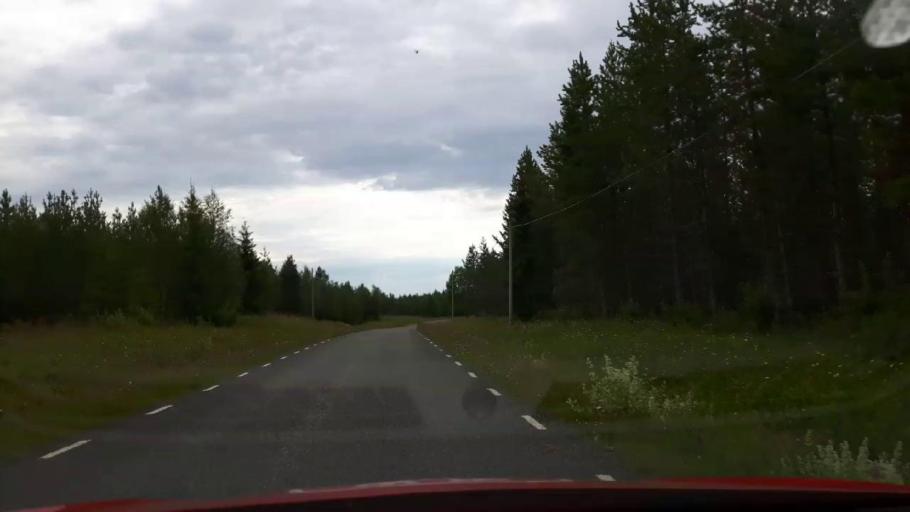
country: SE
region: Jaemtland
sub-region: OEstersunds Kommun
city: Lit
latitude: 63.3830
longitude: 15.0413
